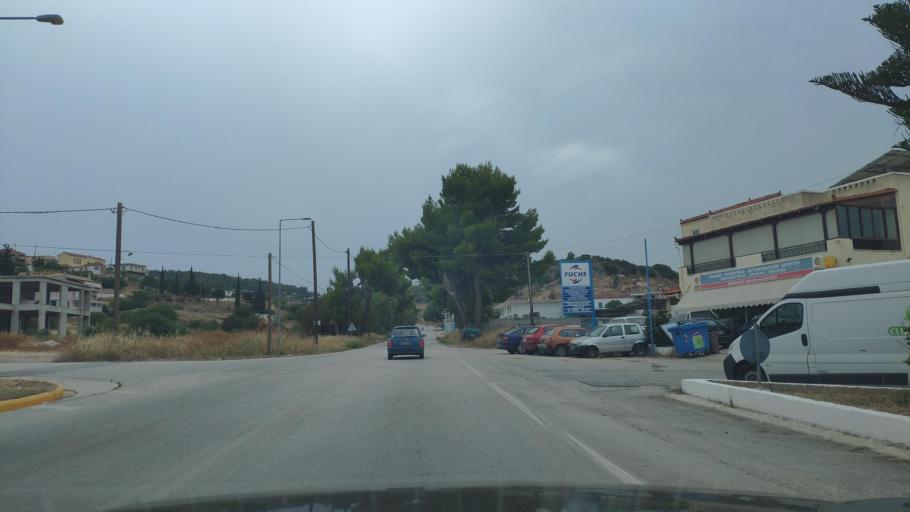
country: GR
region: Peloponnese
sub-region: Nomos Argolidos
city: Kranidi
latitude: 37.3868
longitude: 23.1577
